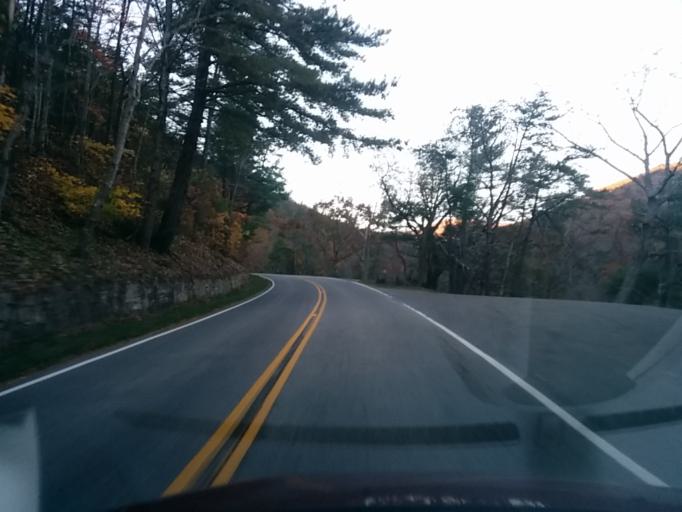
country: US
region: Virginia
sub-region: Rockbridge County
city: East Lexington
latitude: 37.9313
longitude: -79.4485
